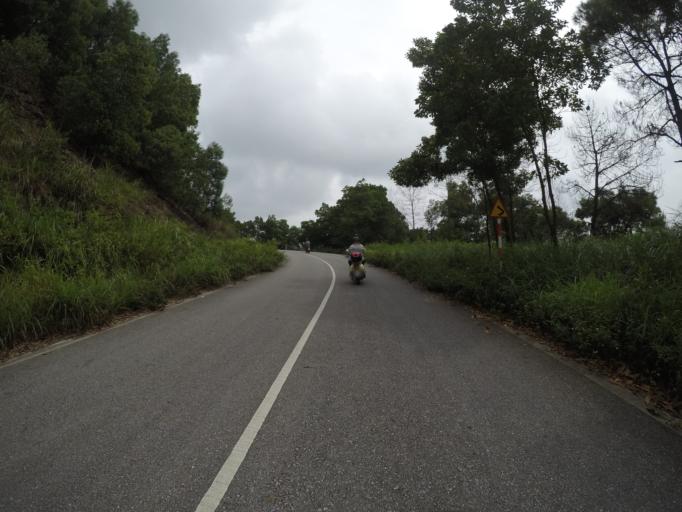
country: VN
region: Ha Noi
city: Soc Son
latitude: 21.2886
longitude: 105.8245
